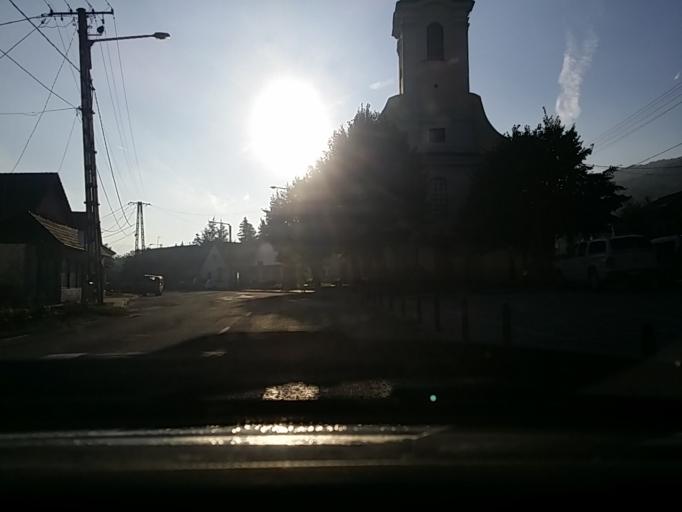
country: HU
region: Komarom-Esztergom
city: Pilismarot
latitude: 47.7638
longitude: 18.9107
